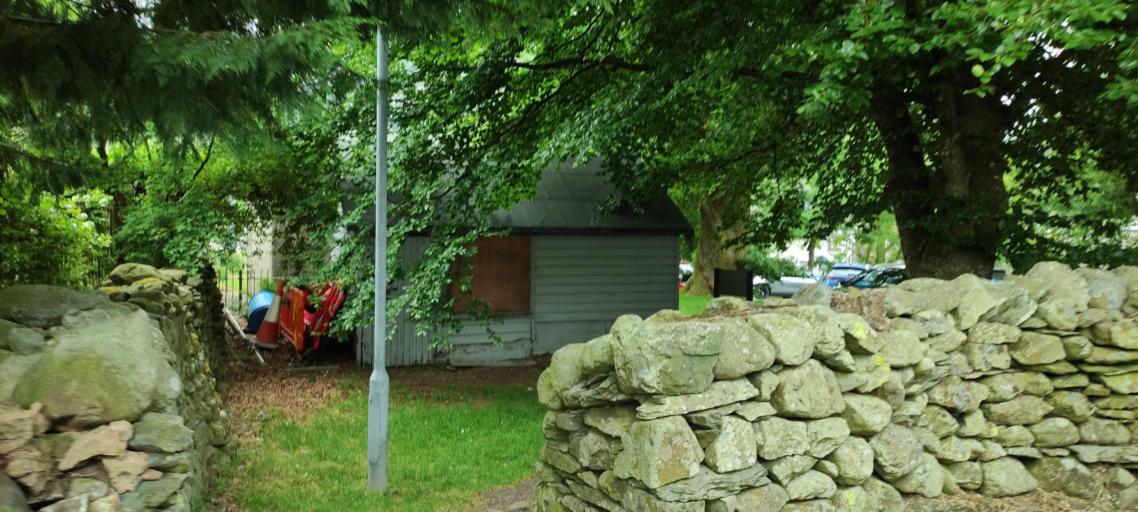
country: GB
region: England
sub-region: Cumbria
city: Ambleside
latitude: 54.5440
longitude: -2.9523
